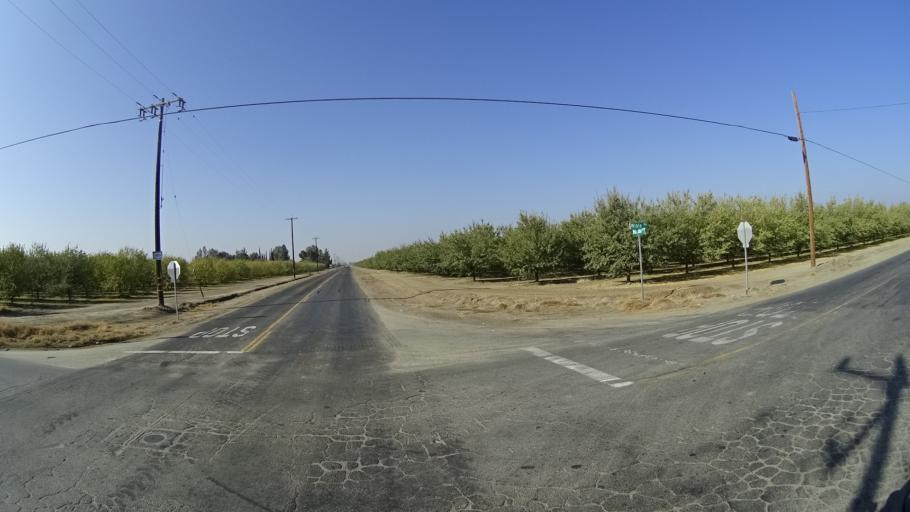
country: US
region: California
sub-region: Kern County
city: Greenfield
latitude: 35.2379
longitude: -119.0388
